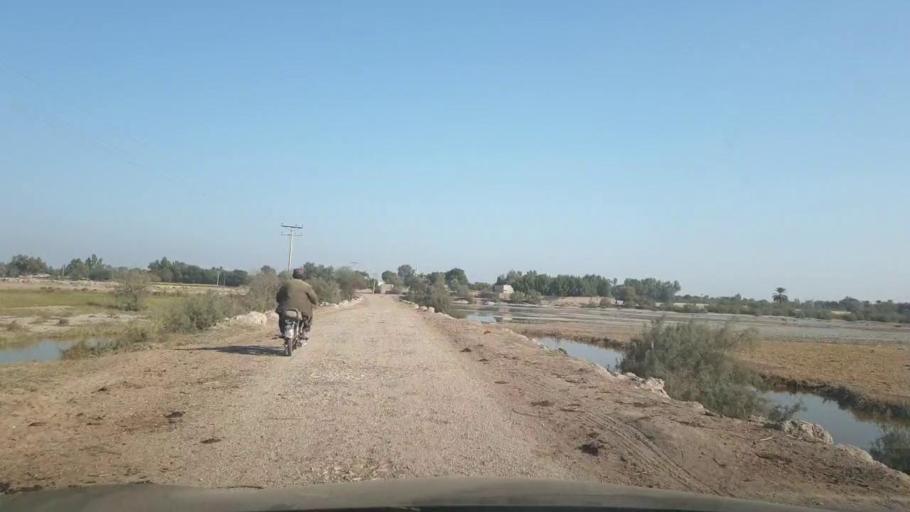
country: PK
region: Sindh
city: Khairpur
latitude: 28.1433
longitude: 69.6000
